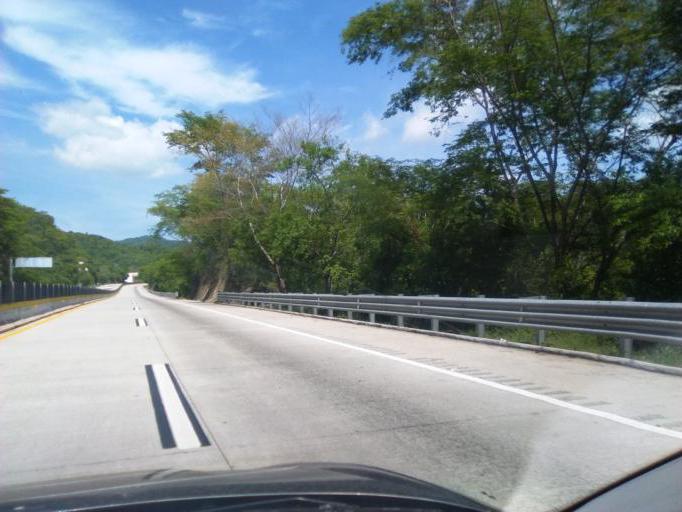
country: MX
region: Guerrero
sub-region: Acapulco de Juarez
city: Colonia Nueva Revolucion
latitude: 16.9366
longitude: -99.7819
